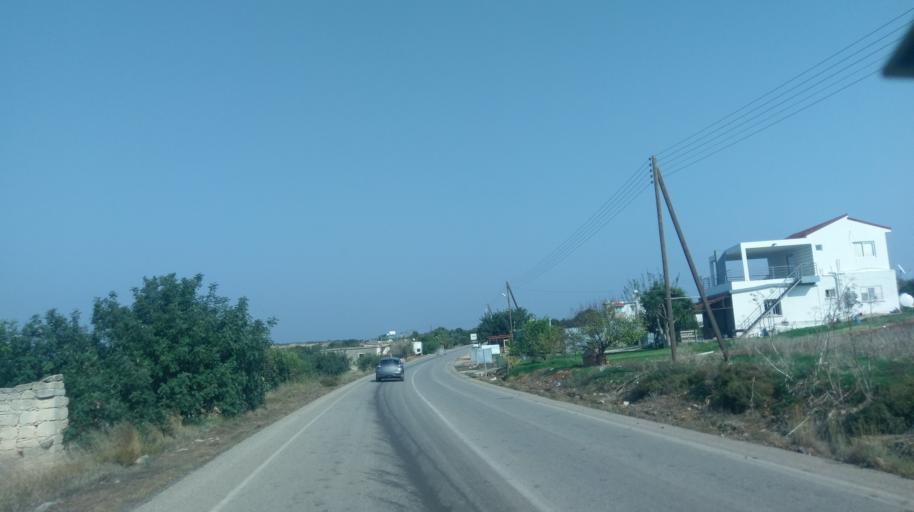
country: CY
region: Ammochostos
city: Leonarisso
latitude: 35.5112
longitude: 34.1614
